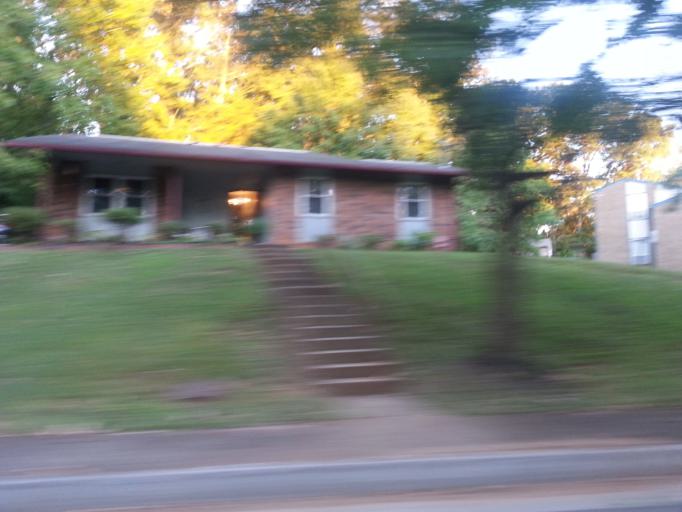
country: US
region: Tennessee
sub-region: Knox County
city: Knoxville
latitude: 35.9679
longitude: -83.8990
